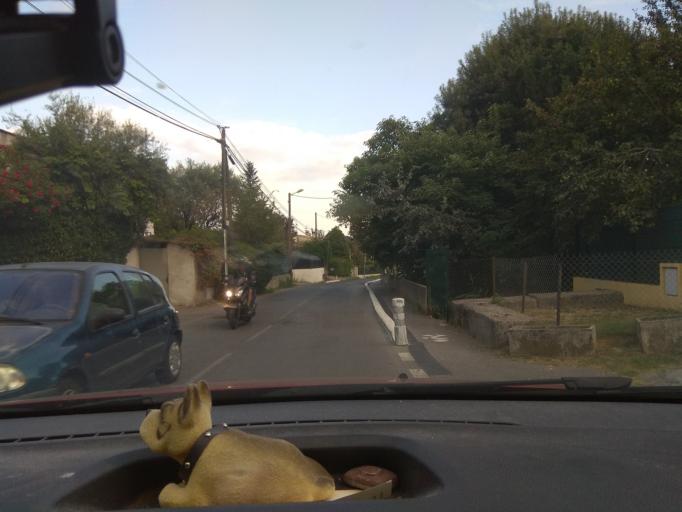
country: FR
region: Provence-Alpes-Cote d'Azur
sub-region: Departement des Alpes-Maritimes
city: La Colle-sur-Loup
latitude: 43.6770
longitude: 7.1087
